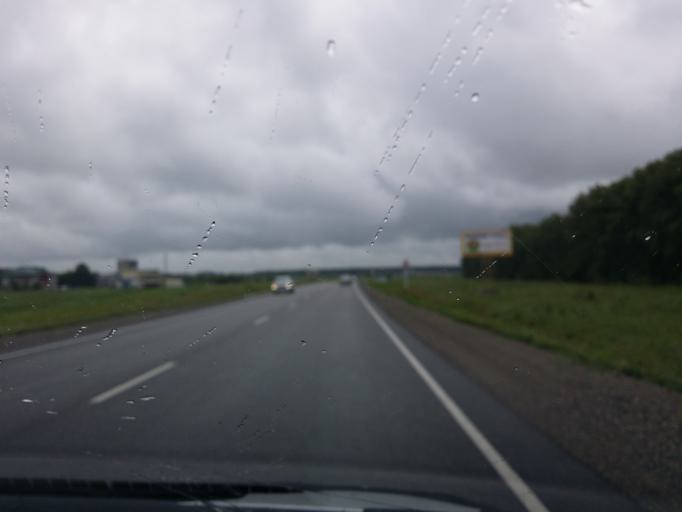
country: RU
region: Altai Krai
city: Zarya
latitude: 52.5887
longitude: 85.1659
